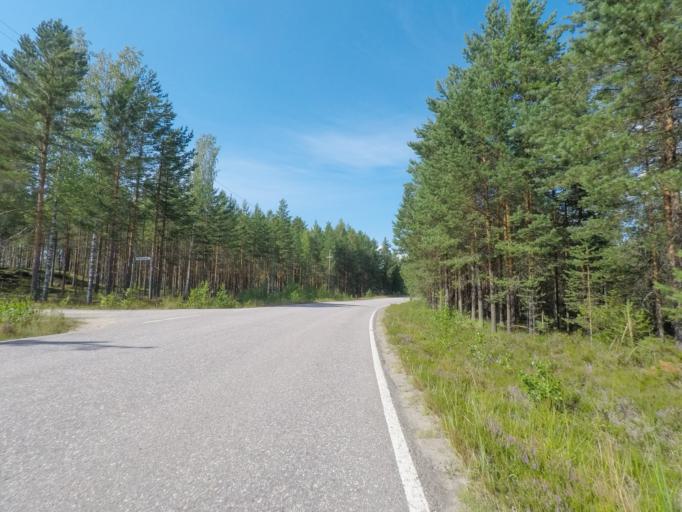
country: FI
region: Southern Savonia
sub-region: Mikkeli
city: Puumala
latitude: 61.4655
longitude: 28.1693
